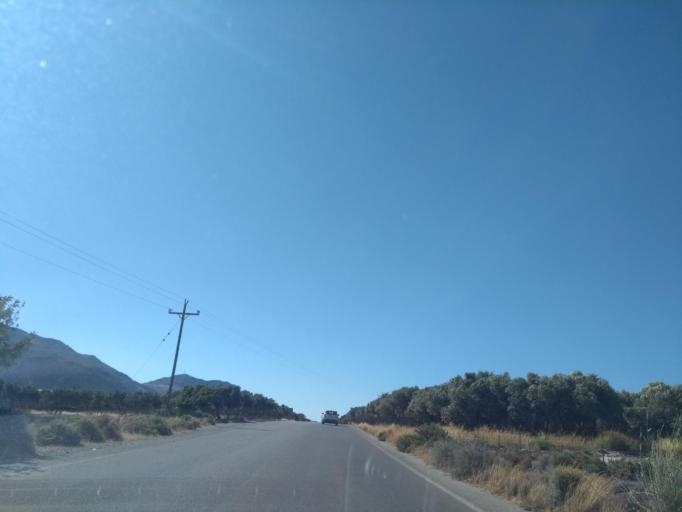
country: GR
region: Crete
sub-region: Nomos Chanias
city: Palaiochora
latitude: 35.2946
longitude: 23.5426
